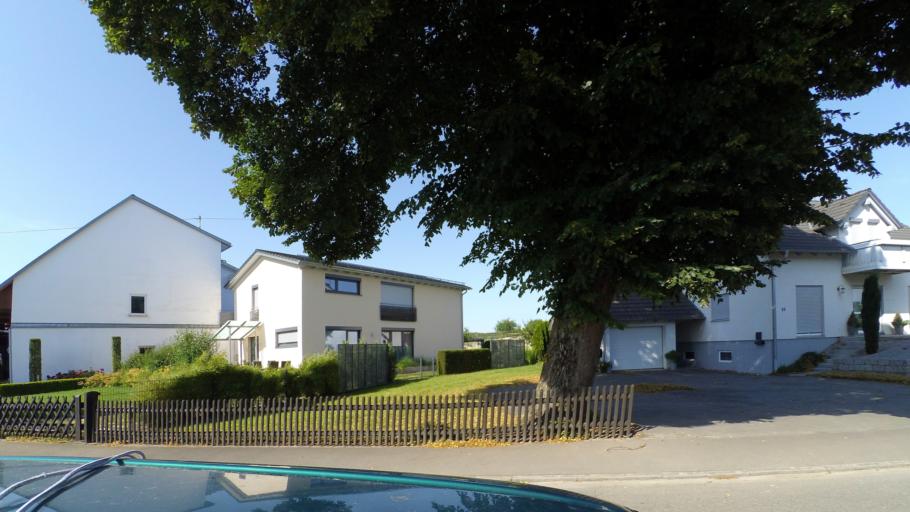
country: DE
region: Baden-Wuerttemberg
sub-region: Regierungsbezirk Stuttgart
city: Hermaringen
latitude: 48.5953
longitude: 10.2647
